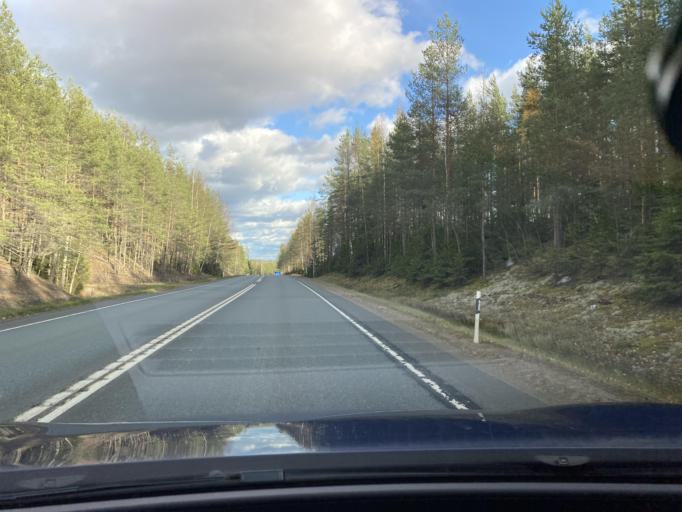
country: FI
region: Haeme
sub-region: Riihimaeki
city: Hausjaervi
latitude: 60.7817
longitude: 24.8838
